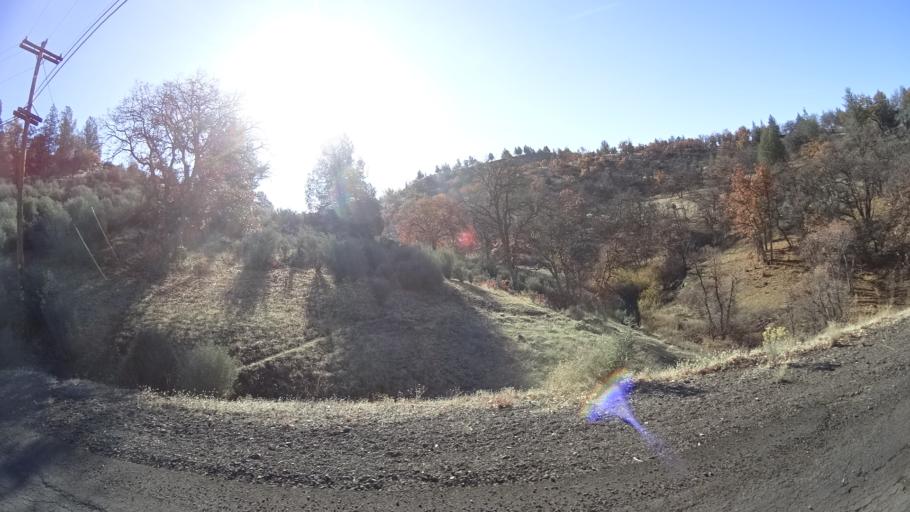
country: US
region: California
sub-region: Siskiyou County
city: Montague
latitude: 41.9142
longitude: -122.4410
